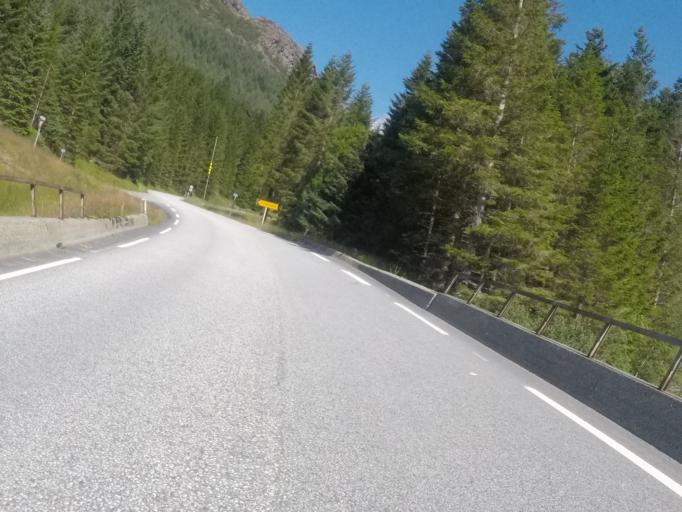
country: NO
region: Sogn og Fjordane
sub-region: Bremanger
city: Svelgen
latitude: 61.6392
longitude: 5.2005
